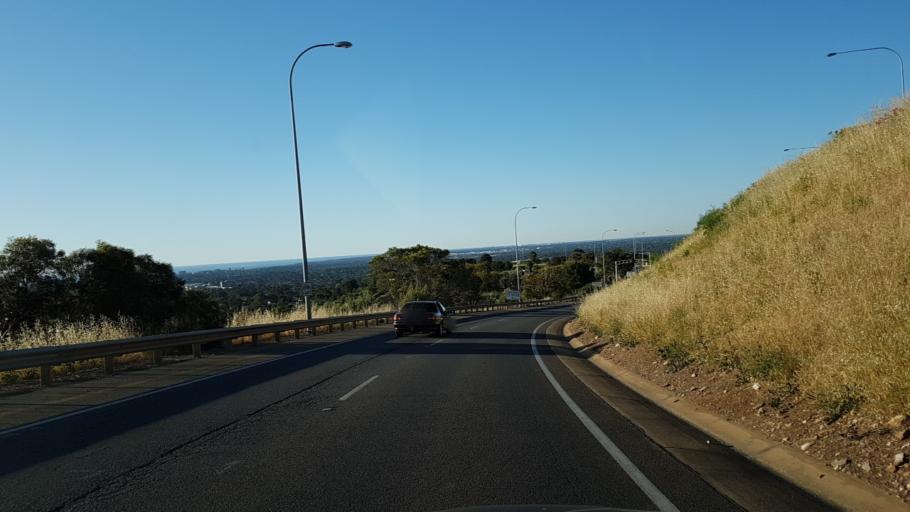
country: AU
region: South Australia
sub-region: Onkaparinga
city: Bedford Park
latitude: -35.0360
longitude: 138.5633
